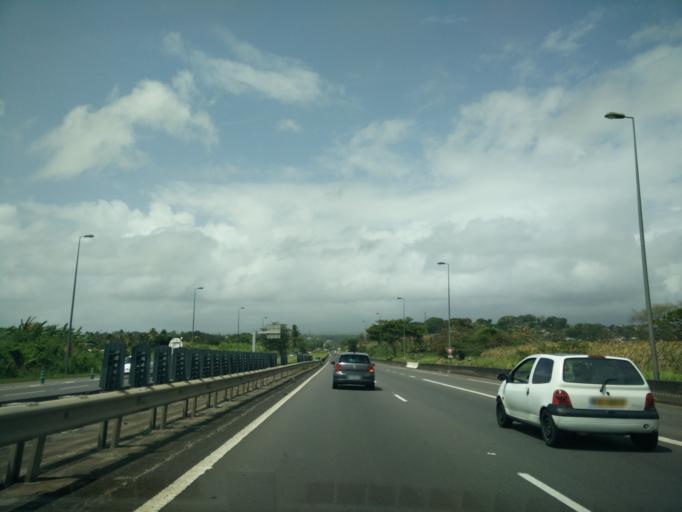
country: GP
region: Guadeloupe
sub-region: Guadeloupe
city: Petit-Bourg
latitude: 16.2162
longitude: -61.5999
